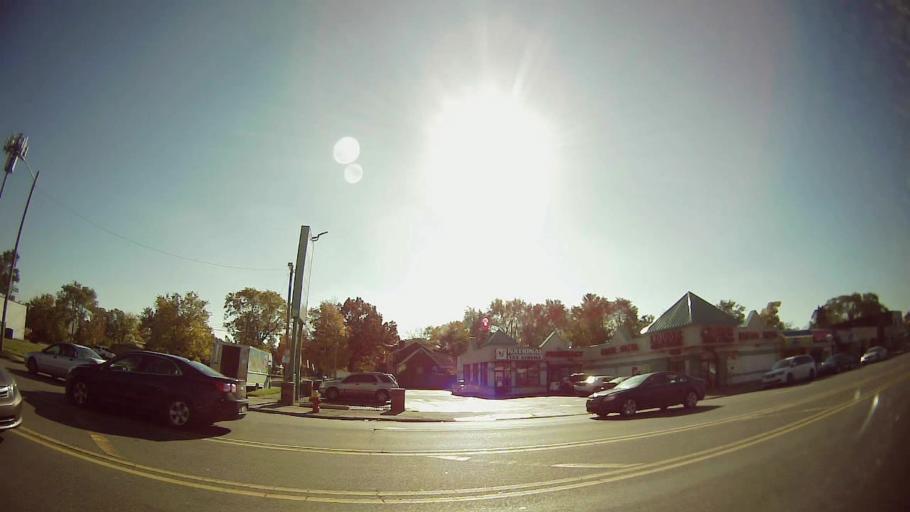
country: US
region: Michigan
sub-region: Oakland County
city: Oak Park
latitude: 42.4161
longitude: -83.2006
